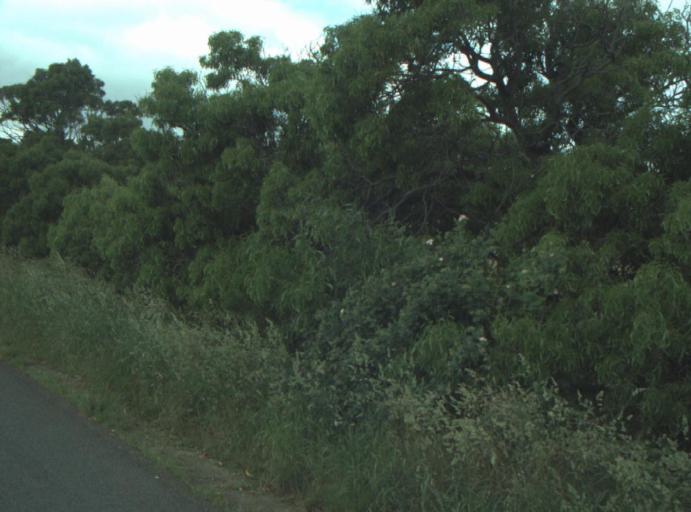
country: AU
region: Victoria
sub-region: Moorabool
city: Bacchus Marsh
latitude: -37.8377
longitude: 144.3560
